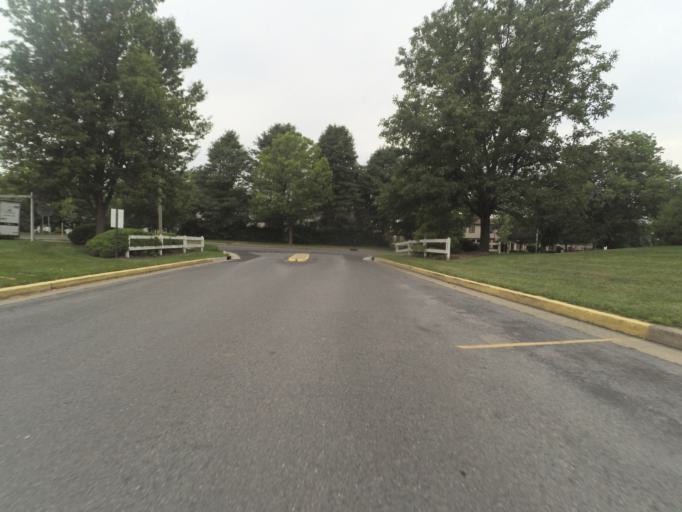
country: US
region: Pennsylvania
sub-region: Centre County
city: State College
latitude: 40.7736
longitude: -77.8609
